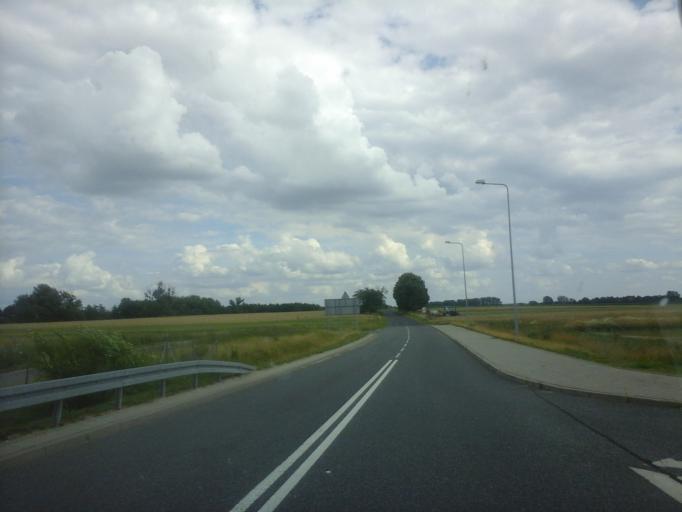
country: PL
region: West Pomeranian Voivodeship
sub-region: Powiat stargardzki
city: Stargard Szczecinski
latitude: 53.3135
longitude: 15.0957
